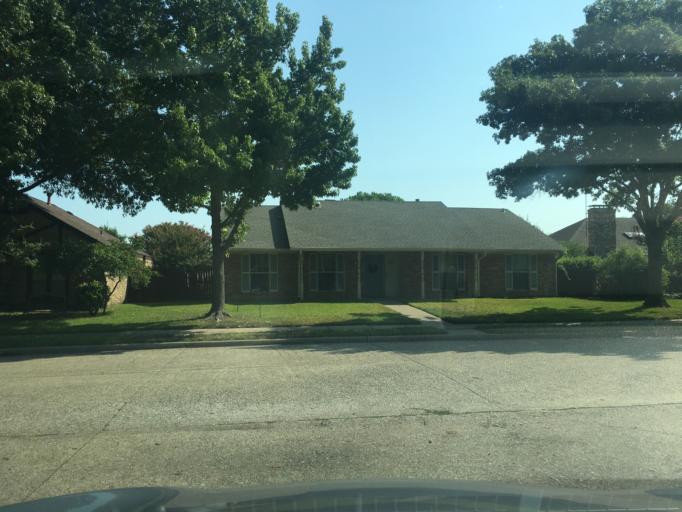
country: US
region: Texas
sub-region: Dallas County
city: Garland
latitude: 32.9411
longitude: -96.6359
